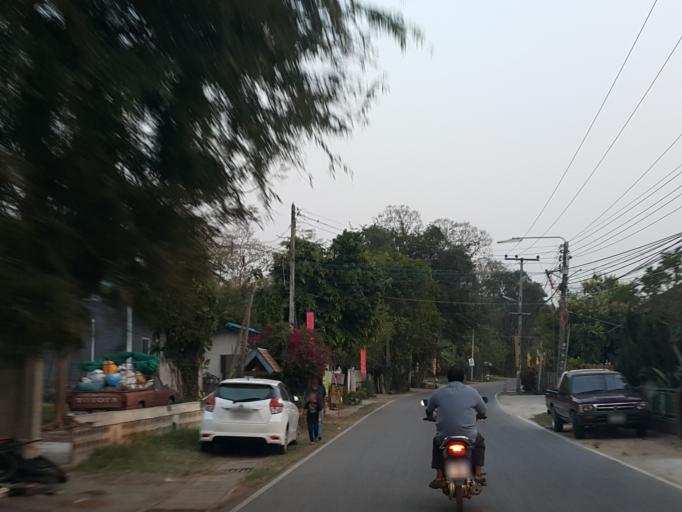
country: TH
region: Chiang Mai
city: Mae Taeng
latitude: 19.0133
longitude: 98.8844
